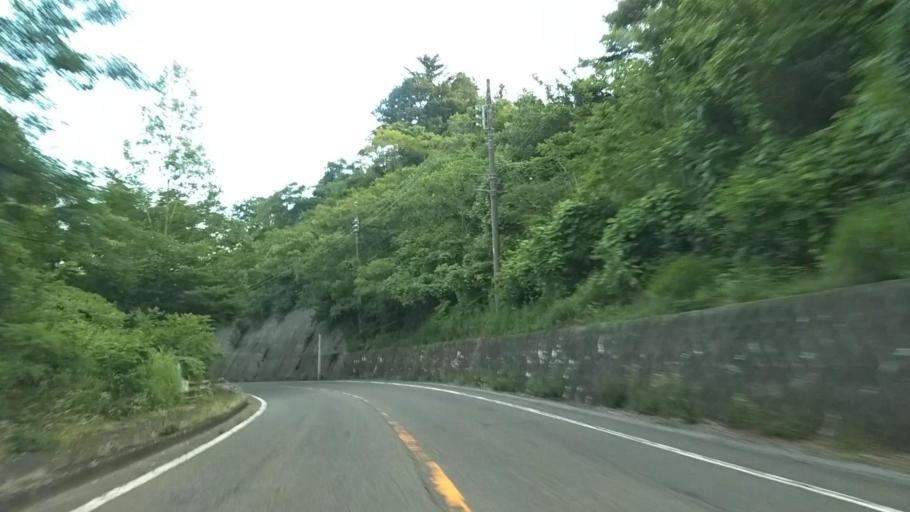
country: JP
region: Yamanashi
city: Uenohara
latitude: 35.5280
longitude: 139.2231
